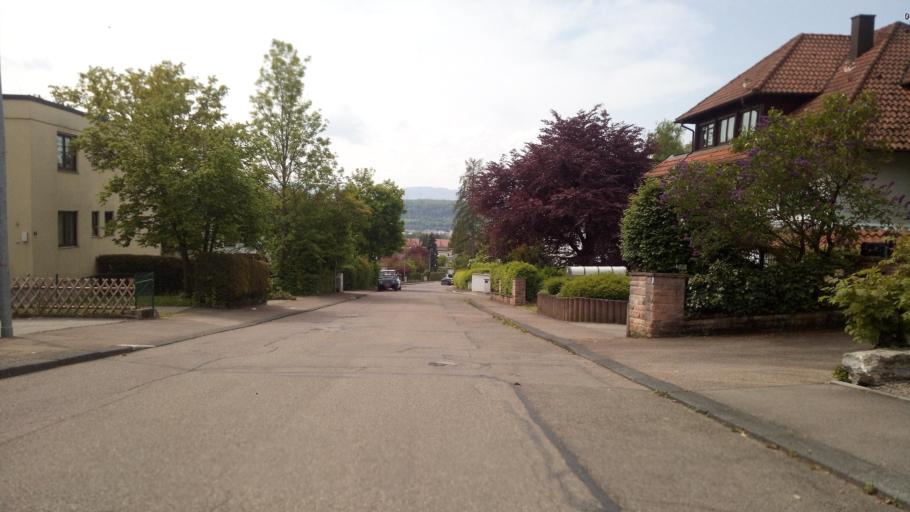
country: DE
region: Baden-Wuerttemberg
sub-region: Regierungsbezirk Stuttgart
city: Goeppingen
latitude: 48.7103
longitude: 9.6657
